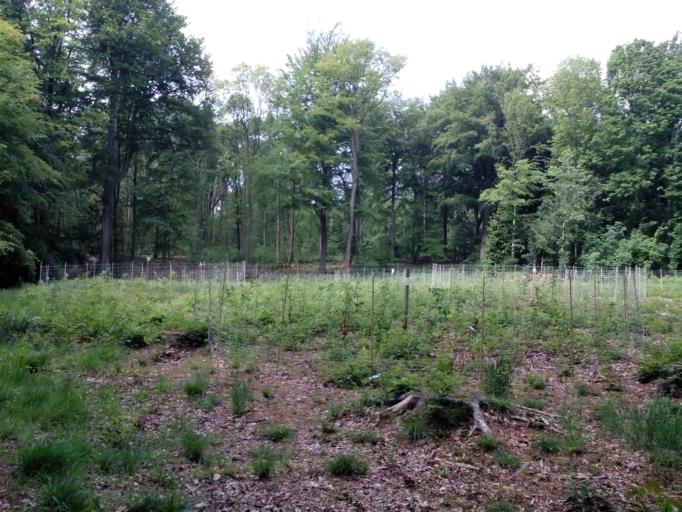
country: BE
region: Flanders
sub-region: Provincie Vlaams-Brabant
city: Bertem
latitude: 50.8779
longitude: 4.6141
